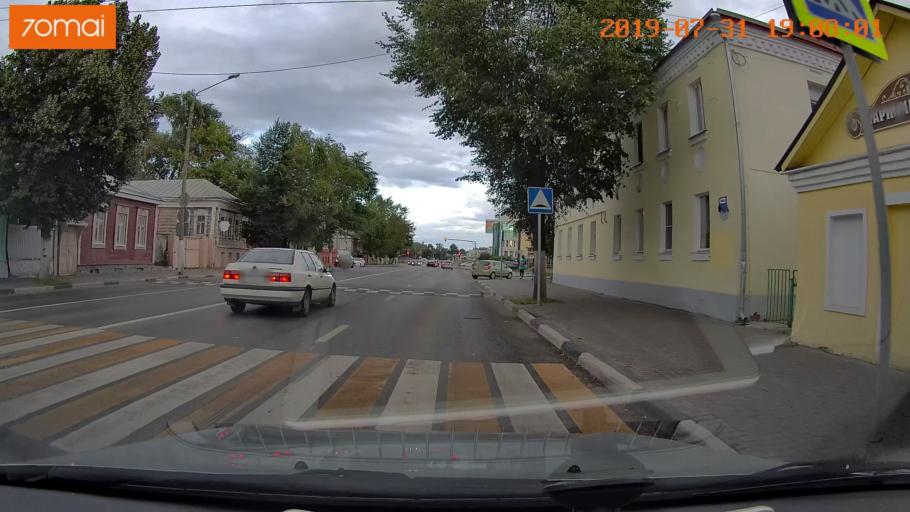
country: RU
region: Moskovskaya
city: Kolomna
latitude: 55.0974
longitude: 38.7622
